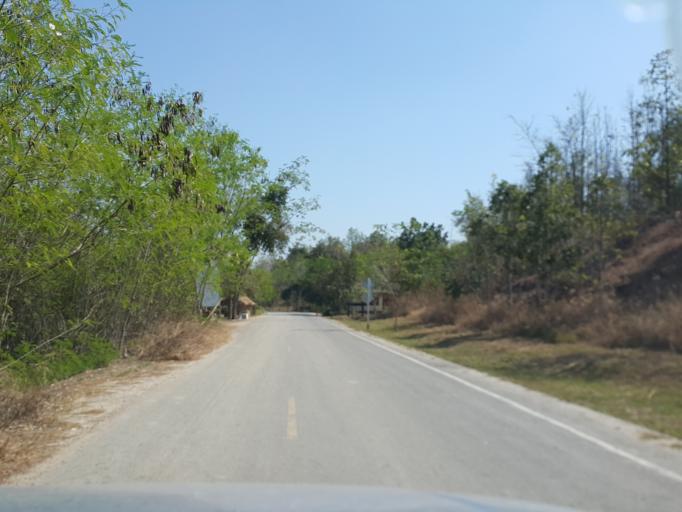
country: TH
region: Chiang Mai
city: Doi Lo
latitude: 18.5278
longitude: 98.7566
